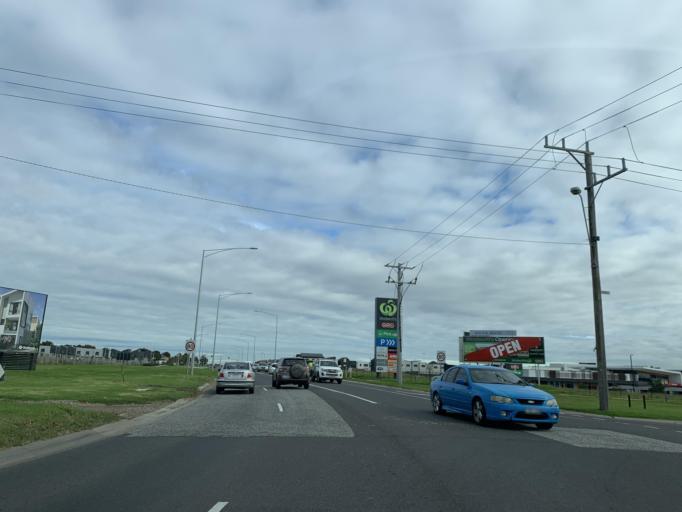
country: AU
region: Victoria
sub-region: Casey
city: Cranbourne West
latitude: -38.1094
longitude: 145.2526
